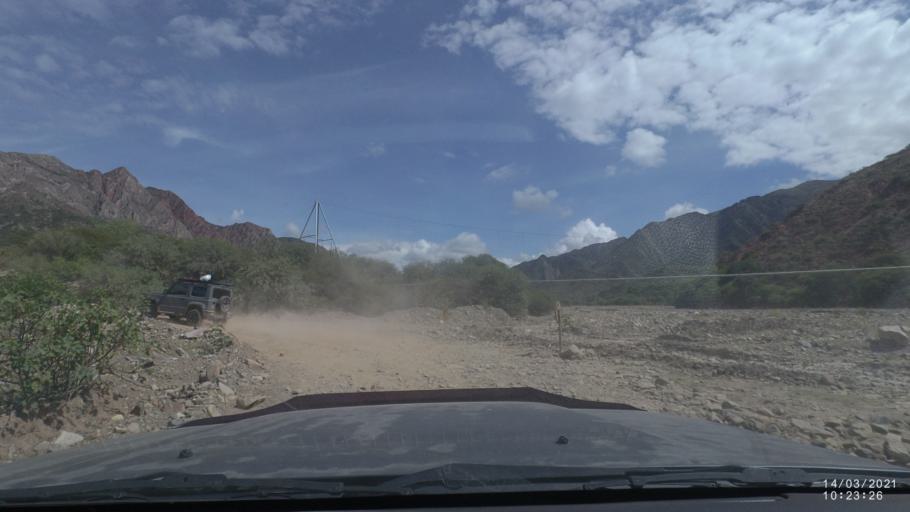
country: BO
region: Cochabamba
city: Cliza
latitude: -17.9171
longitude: -65.8727
